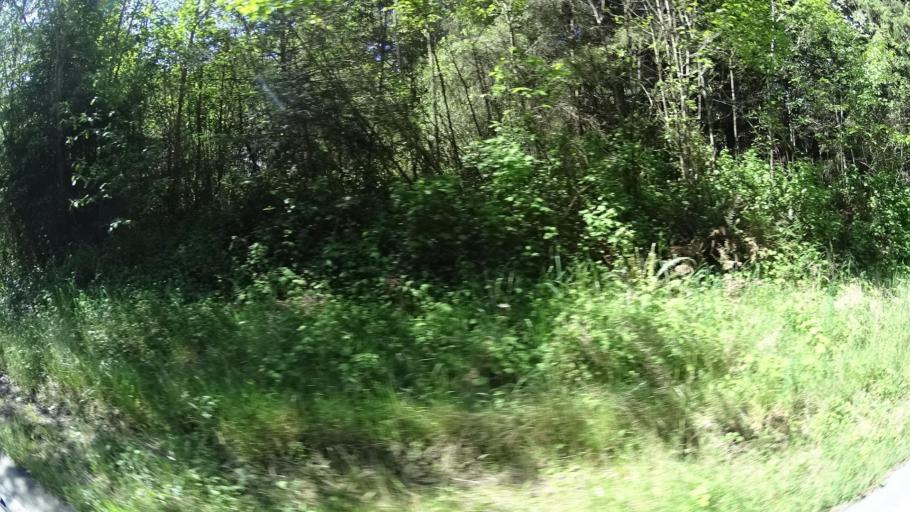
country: US
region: California
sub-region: Humboldt County
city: McKinleyville
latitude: 40.9558
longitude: -124.0866
